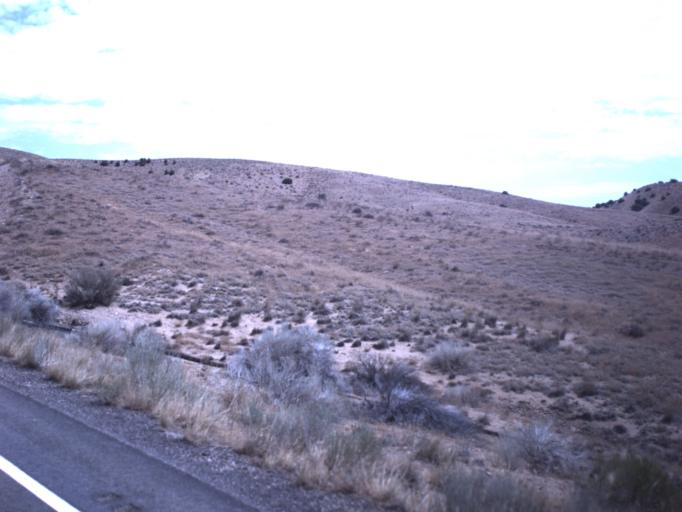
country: US
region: Utah
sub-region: Uintah County
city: Naples
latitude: 40.3352
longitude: -109.4851
